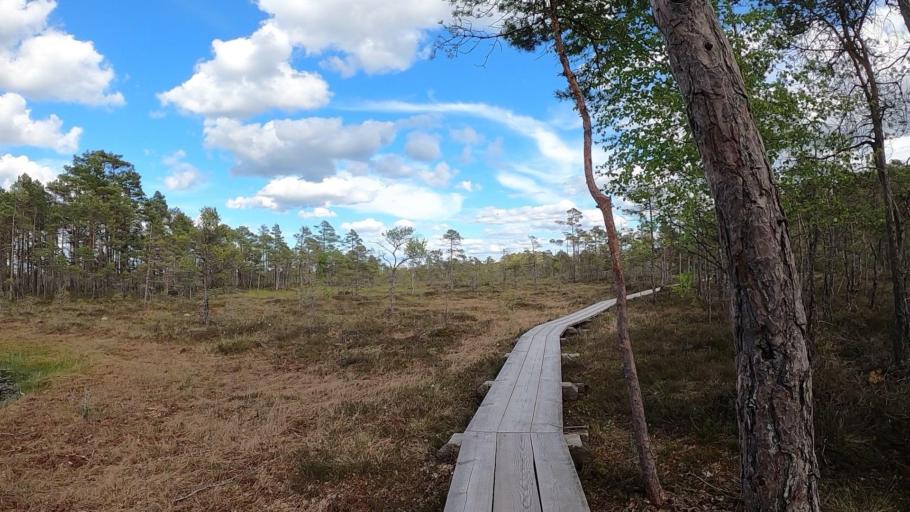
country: LV
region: Jurmala
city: Jurmala
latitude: 56.8538
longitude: 23.8125
